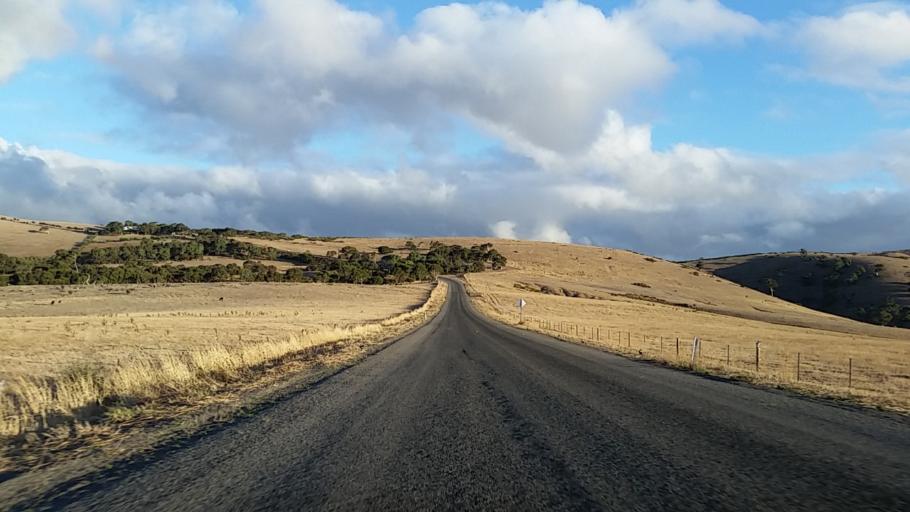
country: AU
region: South Australia
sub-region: Yankalilla
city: Normanville
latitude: -35.5474
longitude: 138.1941
